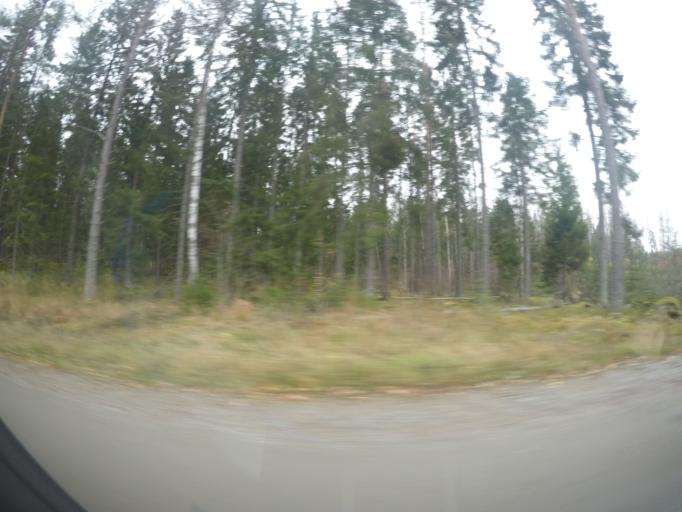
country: SE
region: Vaestmanland
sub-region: Surahammars Kommun
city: Ramnas
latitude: 59.7403
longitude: 16.1319
